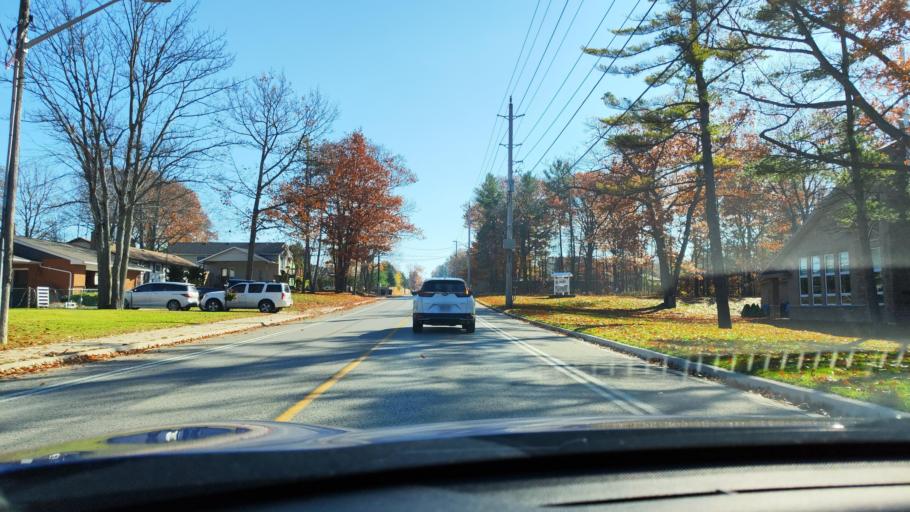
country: CA
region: Ontario
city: Wasaga Beach
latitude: 44.5230
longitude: -79.9991
